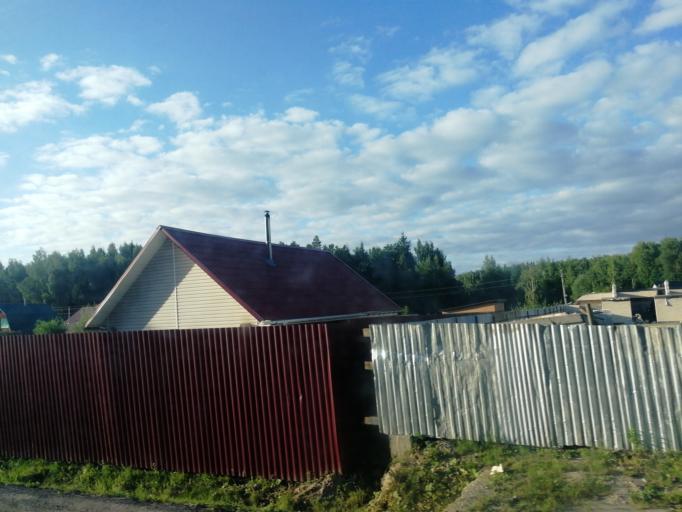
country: RU
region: Kaluga
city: Kaluga
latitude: 54.4507
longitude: 36.3004
